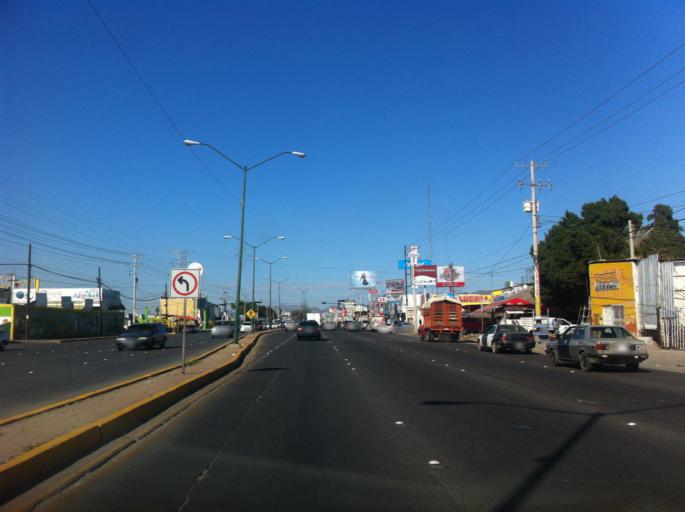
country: MX
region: Sonora
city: Hermosillo
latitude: 29.1124
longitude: -110.9924
